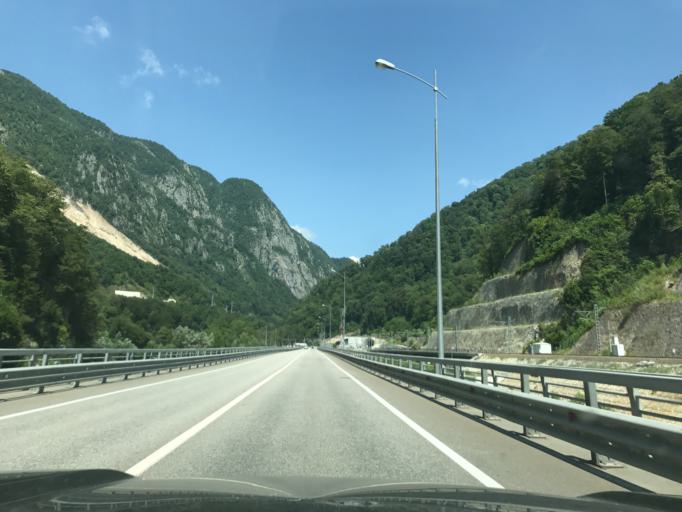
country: RU
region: Krasnodarskiy
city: Vysokoye
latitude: 43.5849
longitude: 40.0115
